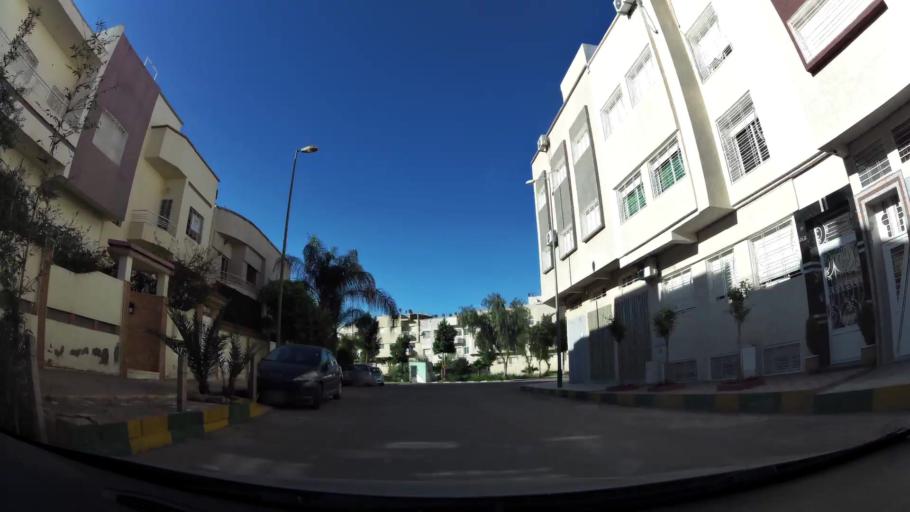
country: MA
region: Fes-Boulemane
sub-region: Fes
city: Fes
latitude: 34.0100
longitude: -5.0134
